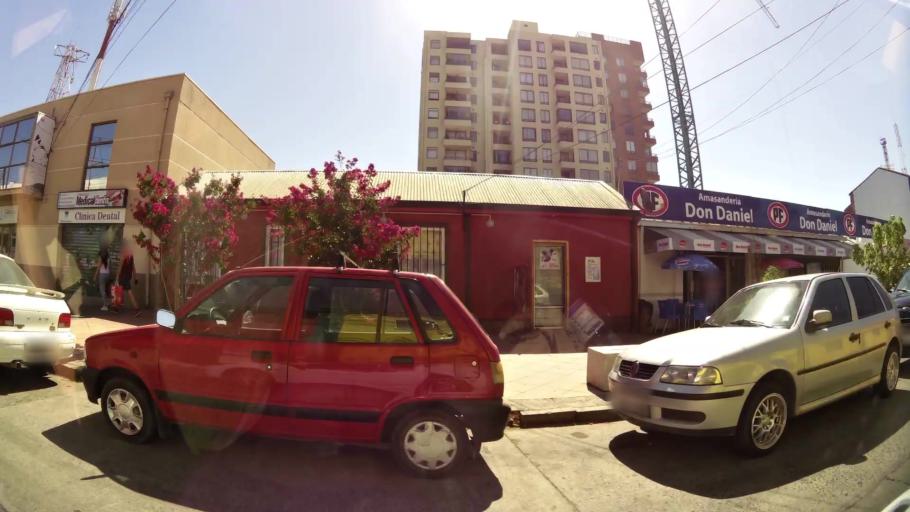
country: CL
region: Maule
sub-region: Provincia de Talca
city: Talca
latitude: -35.4303
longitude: -71.6601
